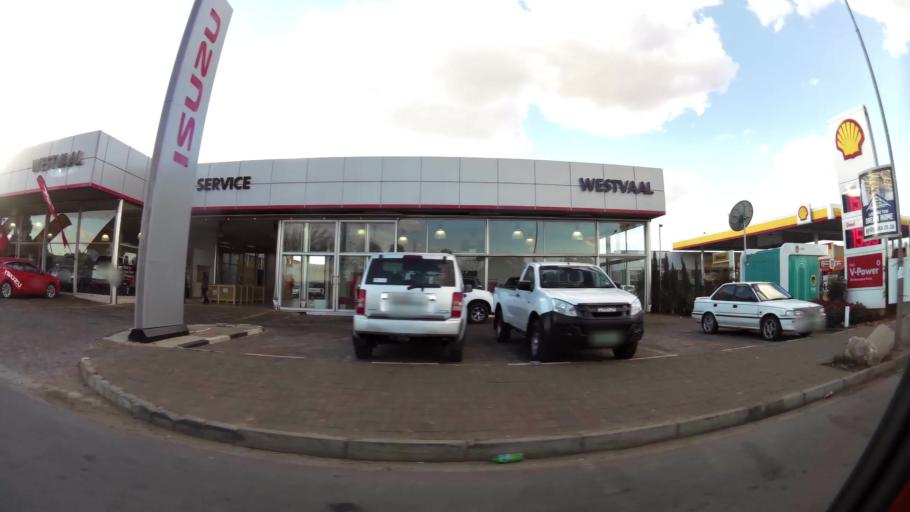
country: ZA
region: North-West
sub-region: Dr Kenneth Kaunda District Municipality
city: Potchefstroom
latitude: -26.7146
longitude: 27.1002
